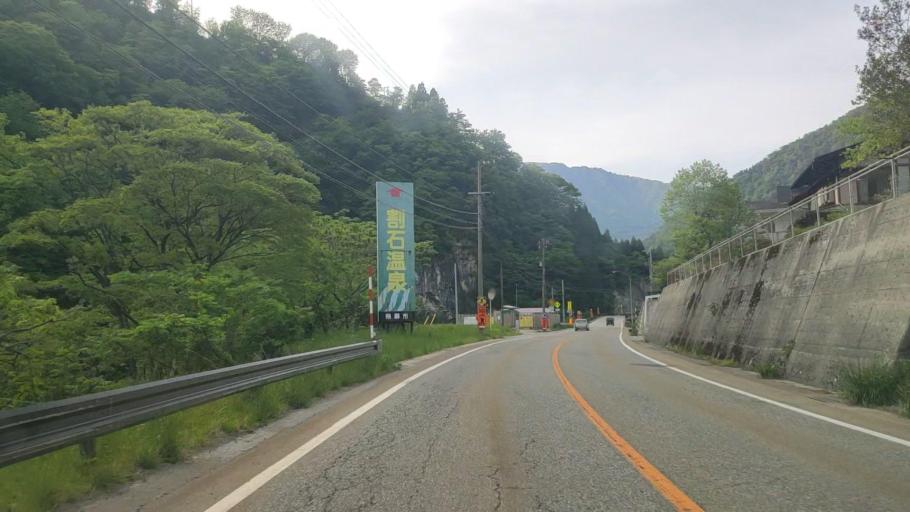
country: JP
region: Gifu
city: Takayama
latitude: 36.3631
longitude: 137.2856
